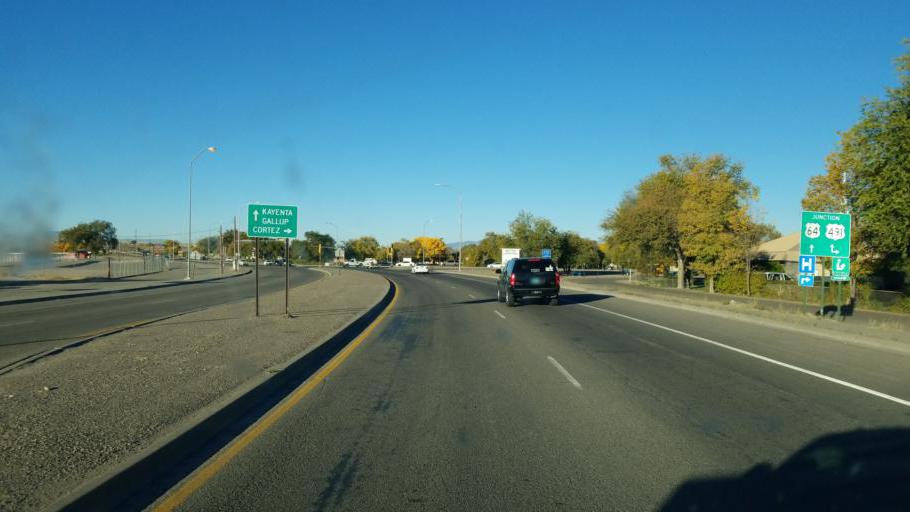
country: US
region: New Mexico
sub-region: San Juan County
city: Shiprock
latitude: 36.7855
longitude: -108.6832
